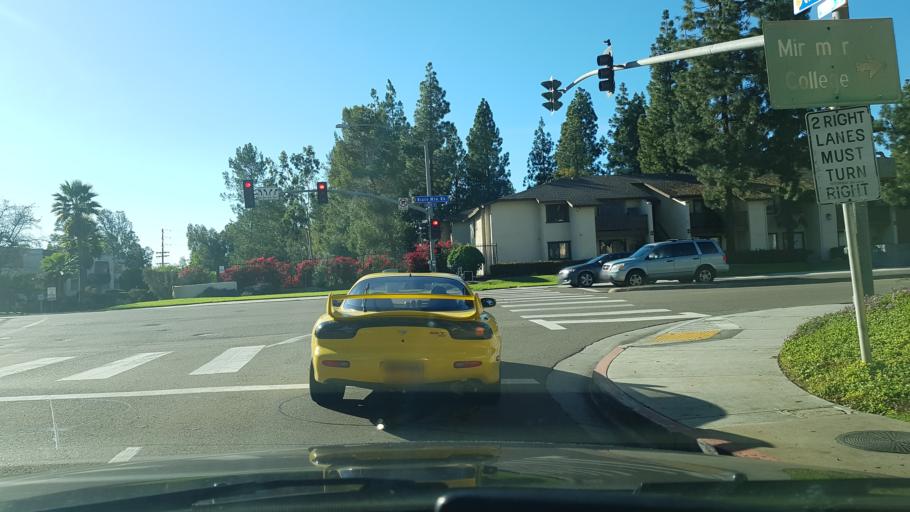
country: US
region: California
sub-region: San Diego County
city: Poway
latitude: 32.9029
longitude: -117.1237
